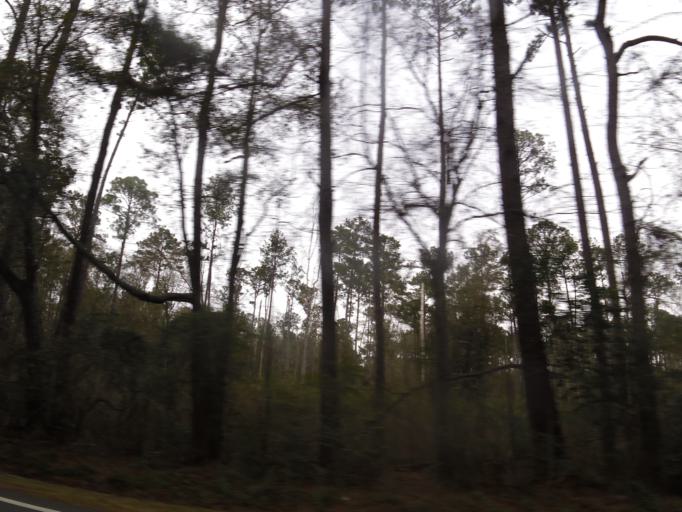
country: US
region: Georgia
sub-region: Thomas County
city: Thomasville
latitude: 30.8516
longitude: -84.0058
